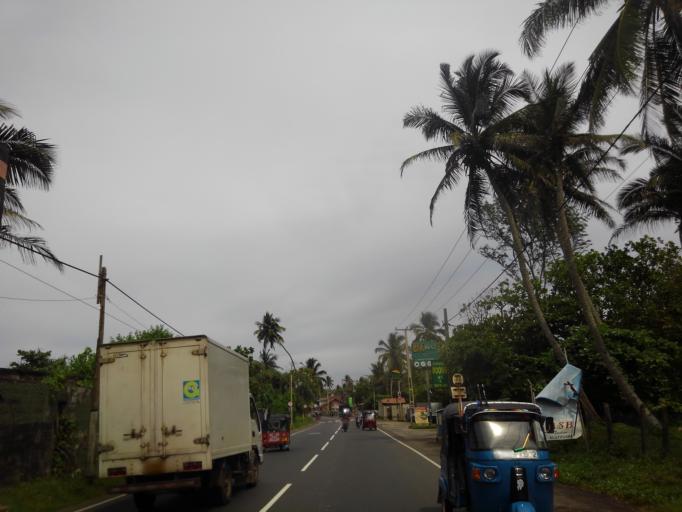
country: LK
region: Western
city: Beruwala
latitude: 6.4825
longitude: 79.9834
